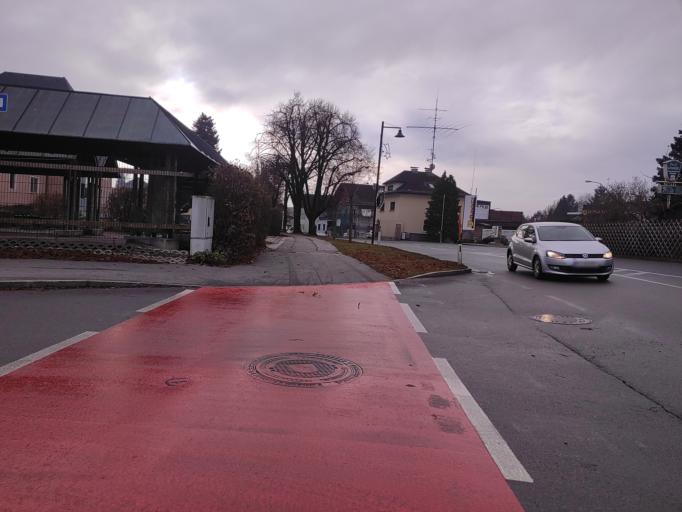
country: AT
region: Salzburg
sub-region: Politischer Bezirk Salzburg-Umgebung
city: Strasswalchen
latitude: 47.9825
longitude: 13.2542
